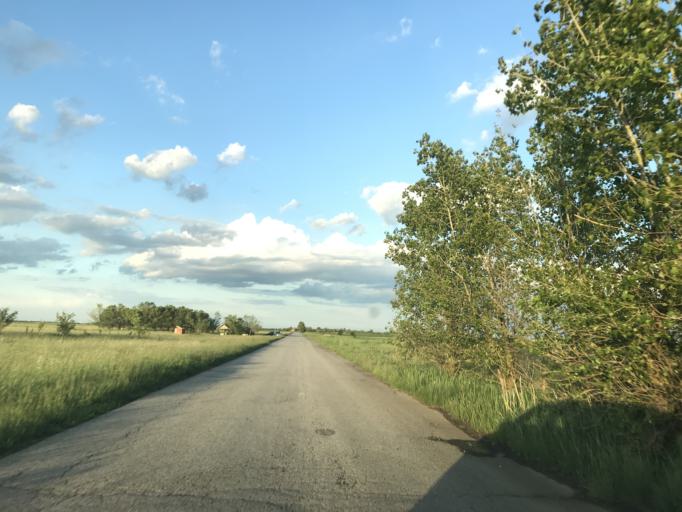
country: RS
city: Banatski Dvor
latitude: 45.5205
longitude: 20.4817
